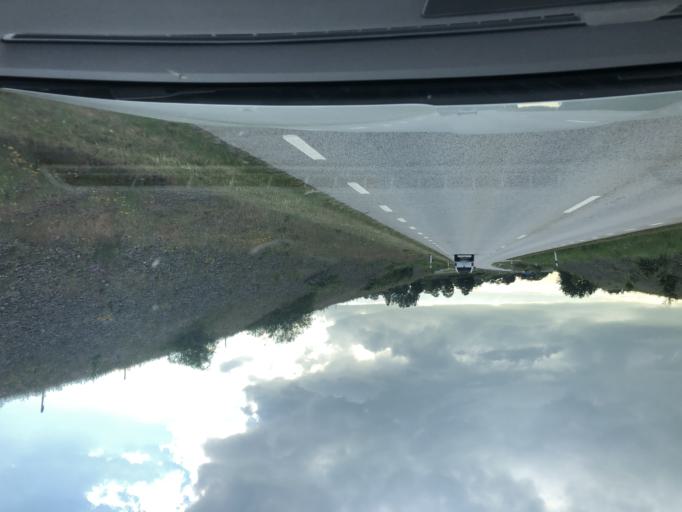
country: SE
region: Skane
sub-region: Simrishamns Kommun
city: Simrishamn
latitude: 55.5357
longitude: 14.2937
